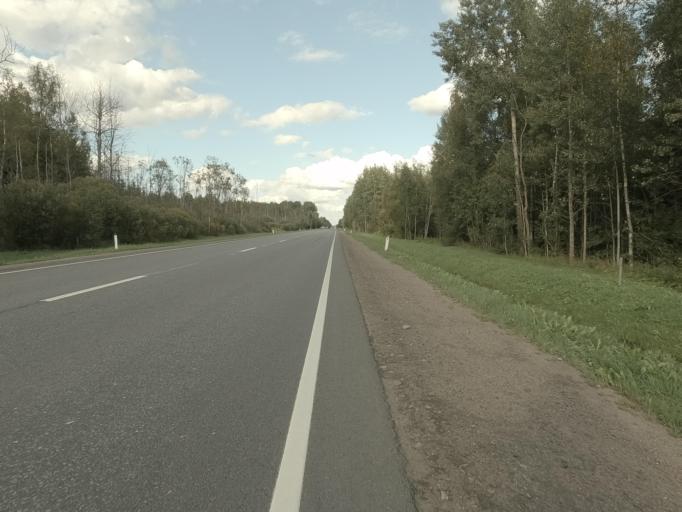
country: RU
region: Leningrad
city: Mga
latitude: 59.6825
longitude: 30.9537
